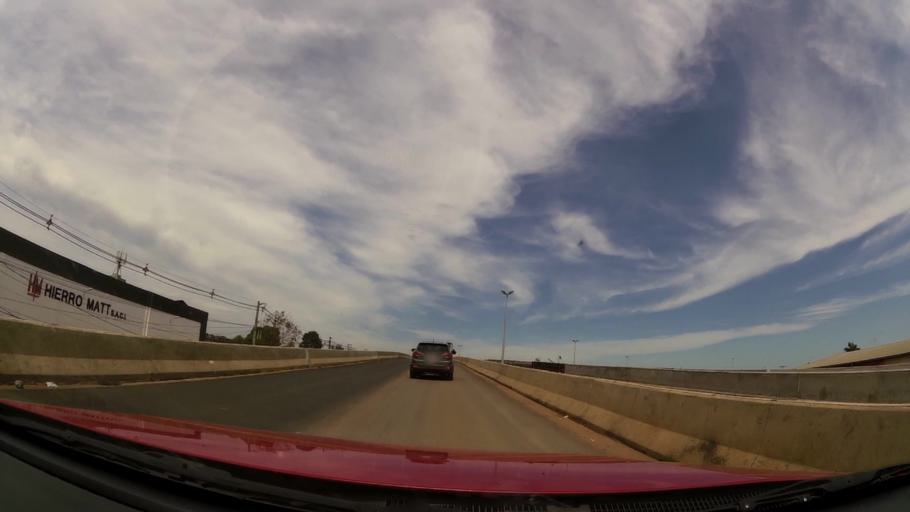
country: PY
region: Central
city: Colonia Mariano Roque Alonso
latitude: -25.2025
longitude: -57.5233
